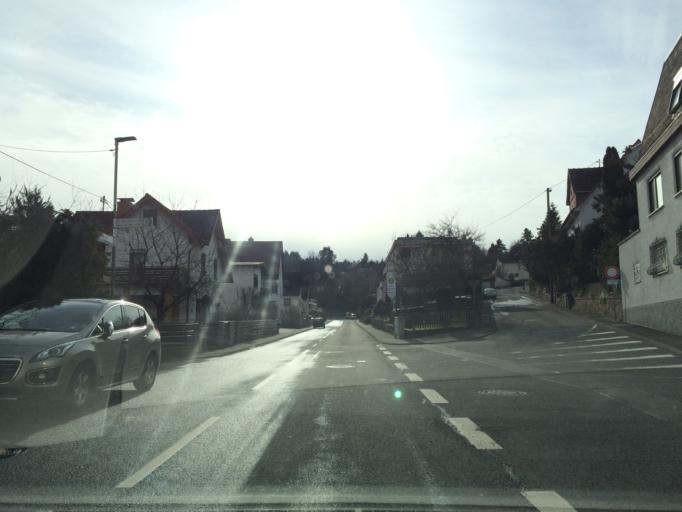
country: DE
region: Hesse
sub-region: Regierungsbezirk Darmstadt
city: Gravenwiesbach
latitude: 50.3576
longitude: 8.4045
